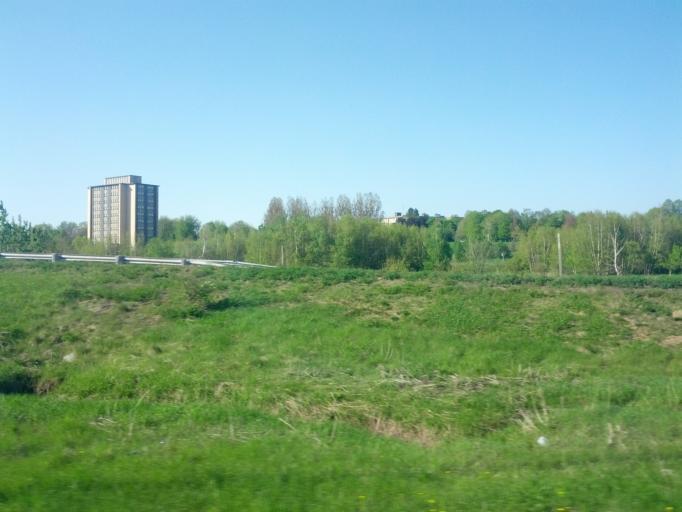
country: CA
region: New Brunswick
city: Moncton
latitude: 46.0998
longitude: -64.7839
